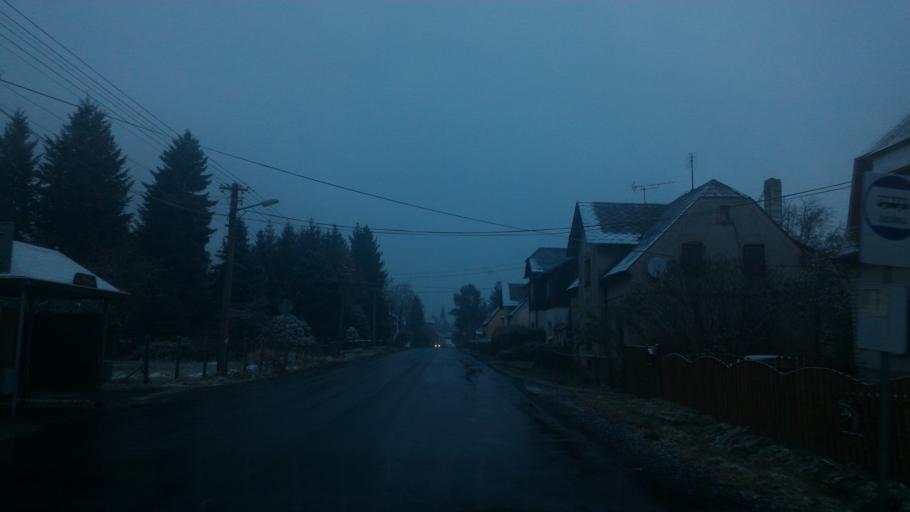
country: CZ
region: Ustecky
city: Jirikov
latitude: 50.9865
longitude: 14.5684
